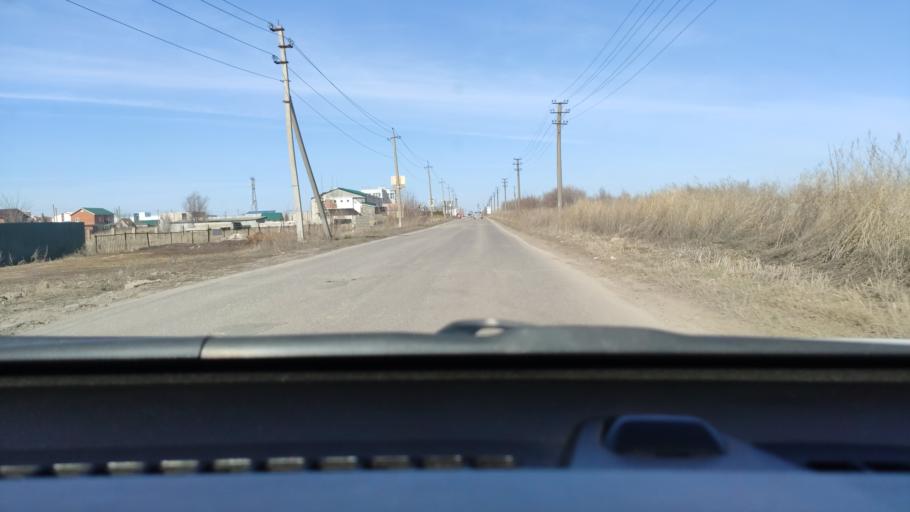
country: RU
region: Samara
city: Podstepki
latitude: 53.5180
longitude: 49.1943
